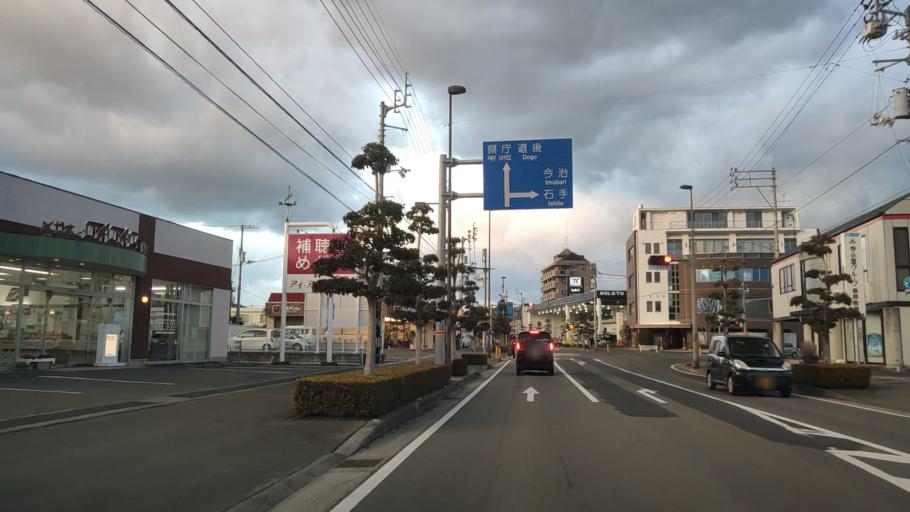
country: JP
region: Ehime
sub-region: Shikoku-chuo Shi
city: Matsuyama
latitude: 33.8367
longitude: 132.7869
